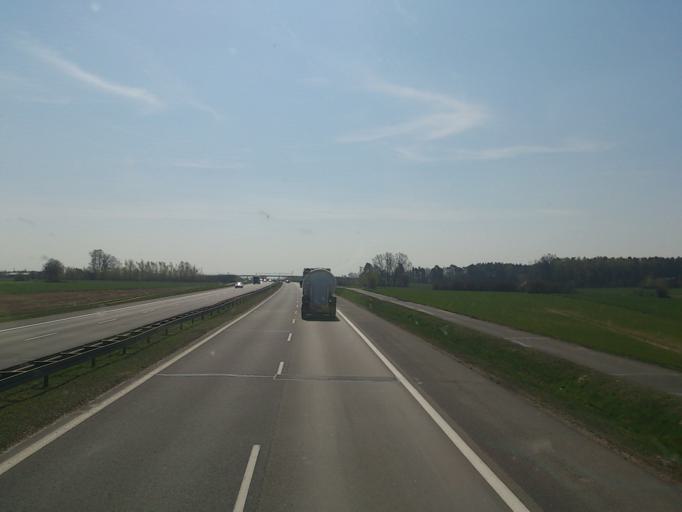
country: PL
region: Lodz Voivodeship
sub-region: Powiat piotrkowski
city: Grabica
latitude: 51.5170
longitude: 19.6003
